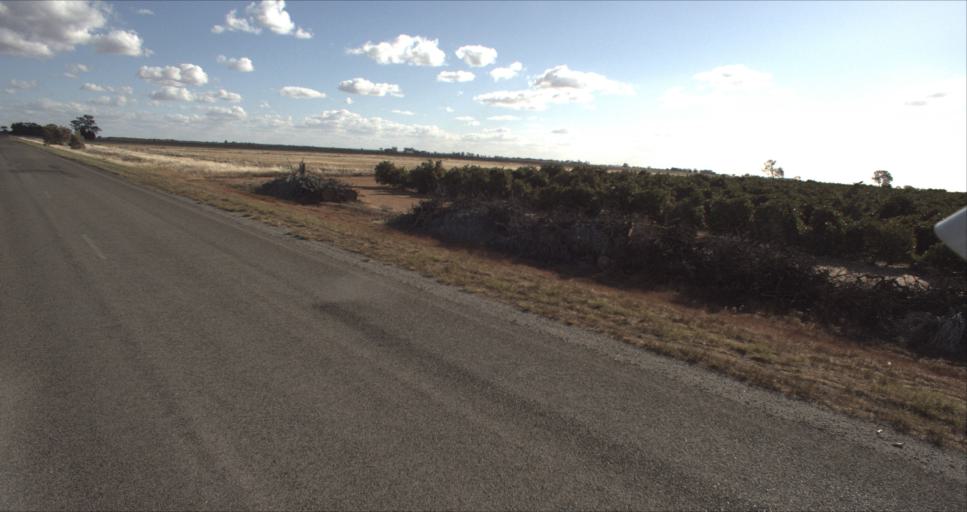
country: AU
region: New South Wales
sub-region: Leeton
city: Leeton
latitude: -34.5295
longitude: 146.2817
